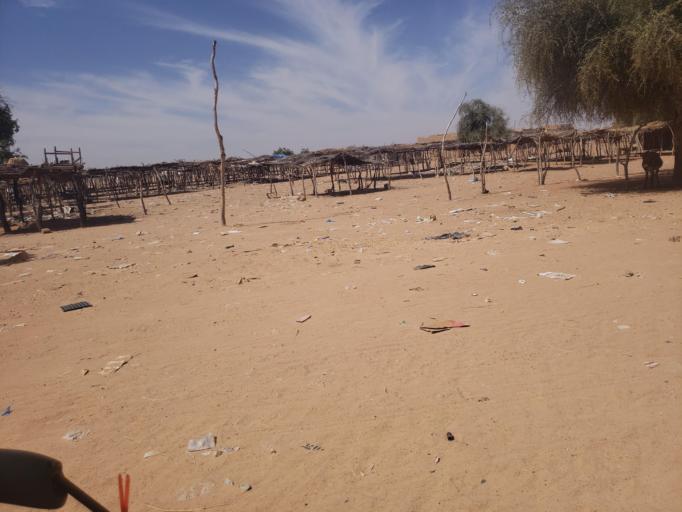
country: SN
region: Matam
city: Ranerou
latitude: 15.2953
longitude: -13.9608
